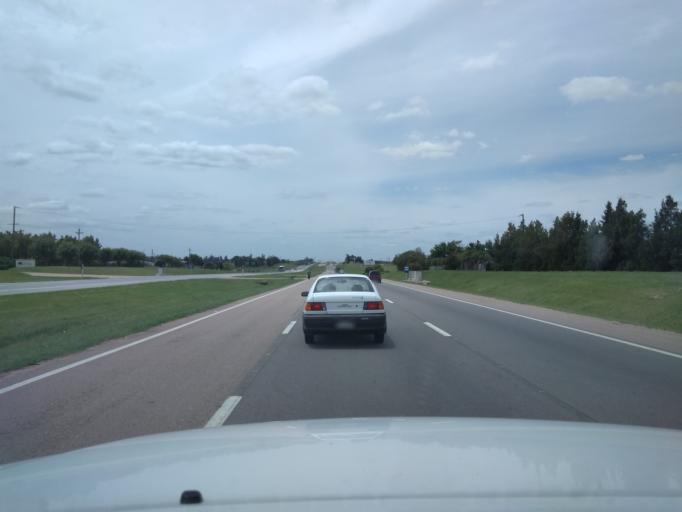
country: UY
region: Canelones
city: Las Piedras
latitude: -34.7389
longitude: -56.2508
